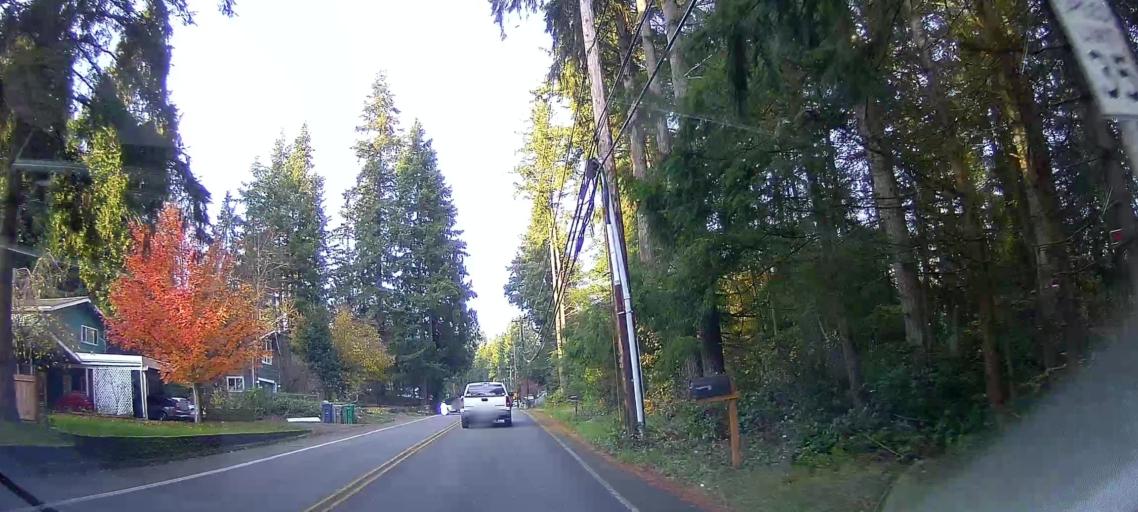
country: US
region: Washington
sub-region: Snohomish County
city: Alderwood Manor
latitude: 47.8138
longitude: -122.2581
